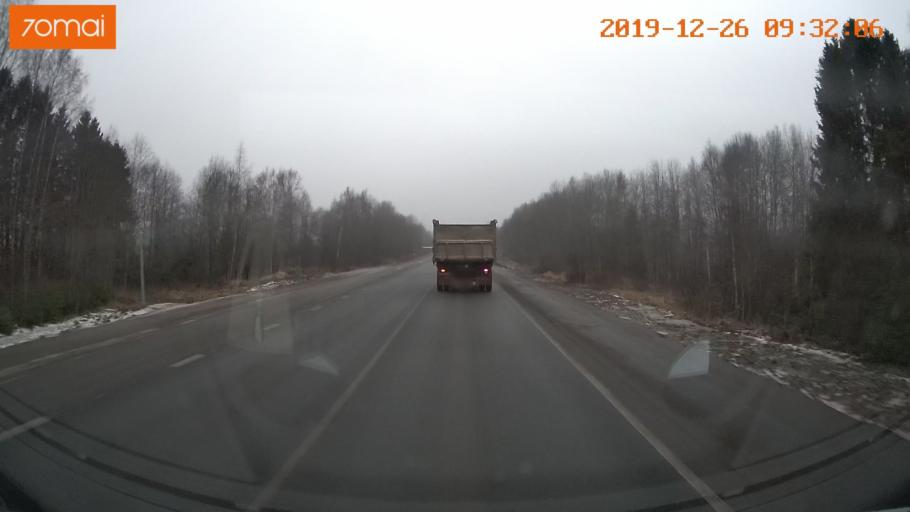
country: RU
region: Vologda
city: Gryazovets
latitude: 59.0747
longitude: 40.1206
